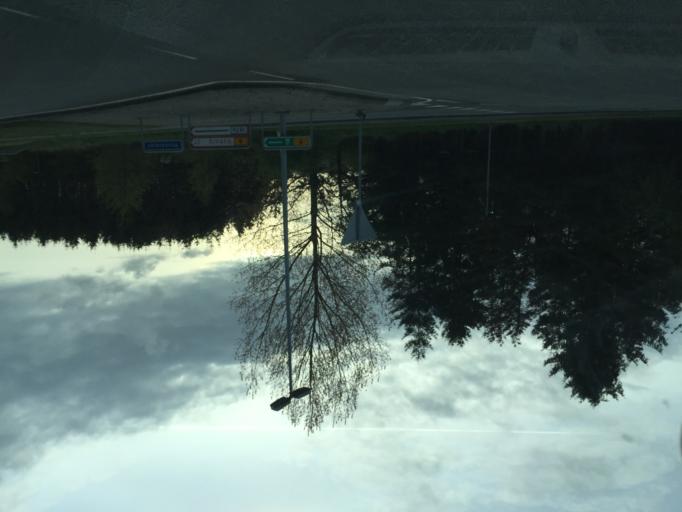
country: DK
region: South Denmark
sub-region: Faaborg-Midtfyn Kommune
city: Ringe
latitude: 55.1816
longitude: 10.5311
